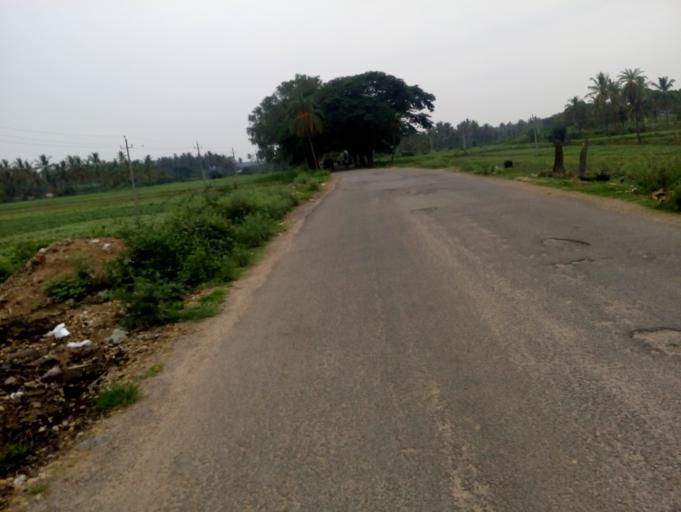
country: IN
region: Karnataka
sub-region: Tumkur
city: Turuvekere
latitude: 13.1771
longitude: 76.6733
